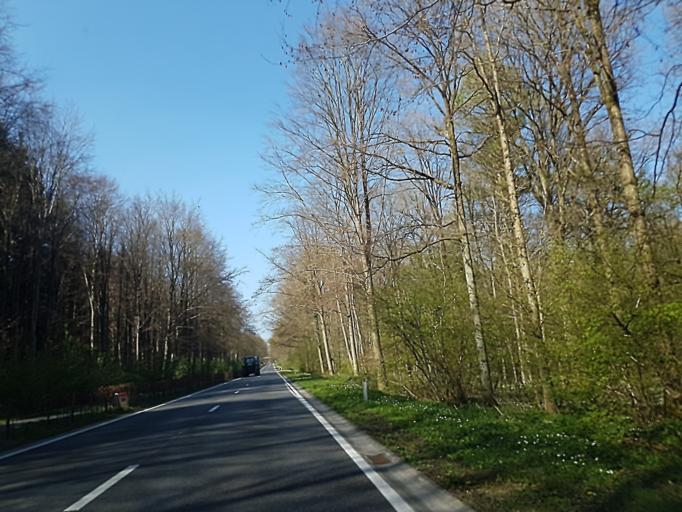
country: BE
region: Flanders
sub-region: Provincie Vlaams-Brabant
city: Oud-Heverlee
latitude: 50.8027
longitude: 4.7084
